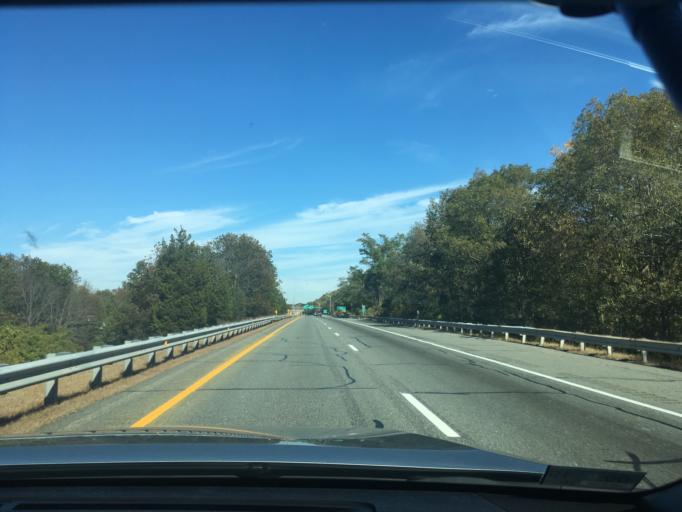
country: US
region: Rhode Island
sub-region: Providence County
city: Cranston
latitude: 41.7472
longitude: -71.4845
